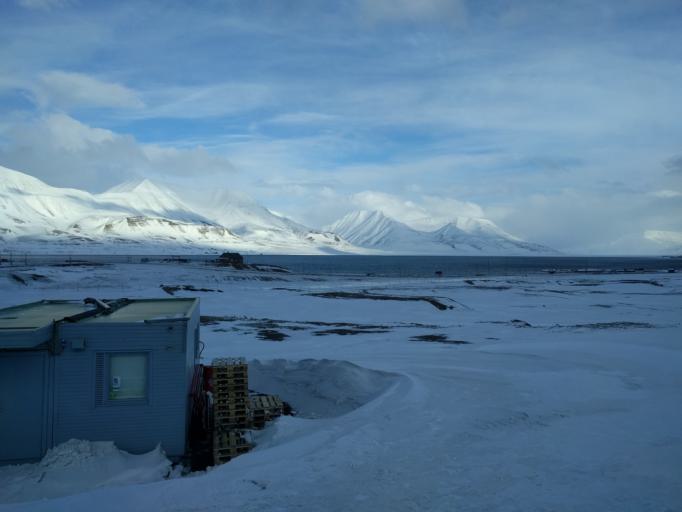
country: SJ
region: Svalbard
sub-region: Spitsbergen
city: Longyearbyen
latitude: 78.2419
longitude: 15.5174
